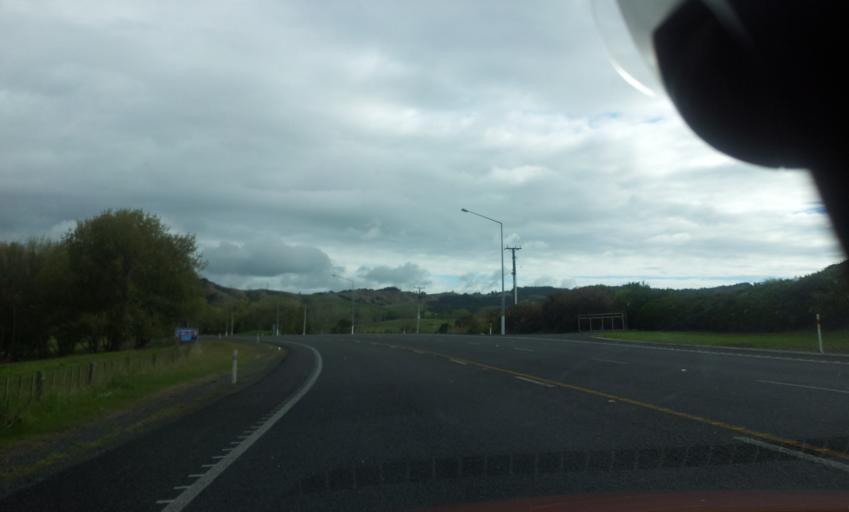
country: NZ
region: Auckland
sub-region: Auckland
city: Wellsford
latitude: -36.2360
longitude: 174.5111
